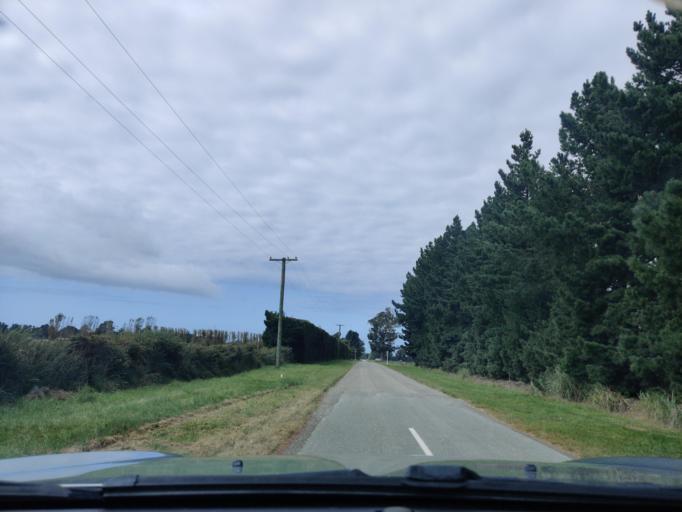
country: NZ
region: Canterbury
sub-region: Hurunui District
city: Amberley
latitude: -43.2189
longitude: 172.7036
